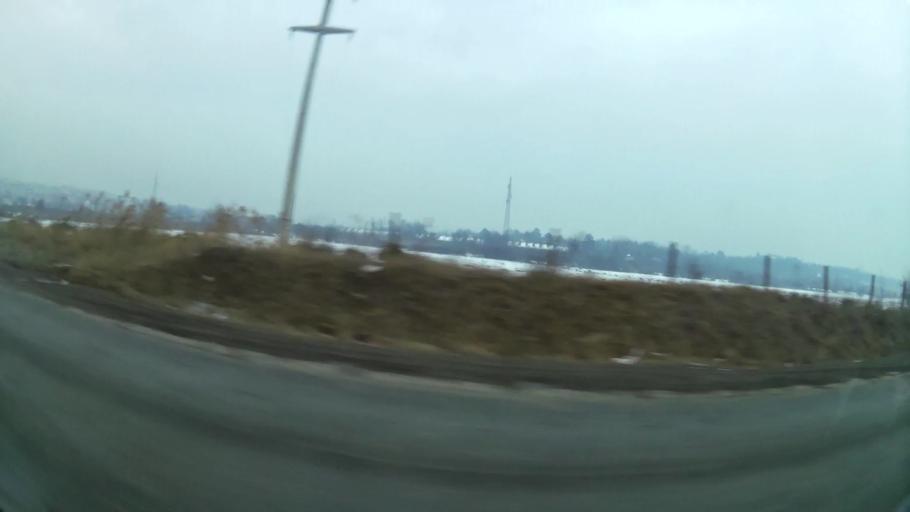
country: MK
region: Suto Orizari
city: Suto Orizare
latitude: 42.0234
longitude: 21.4093
